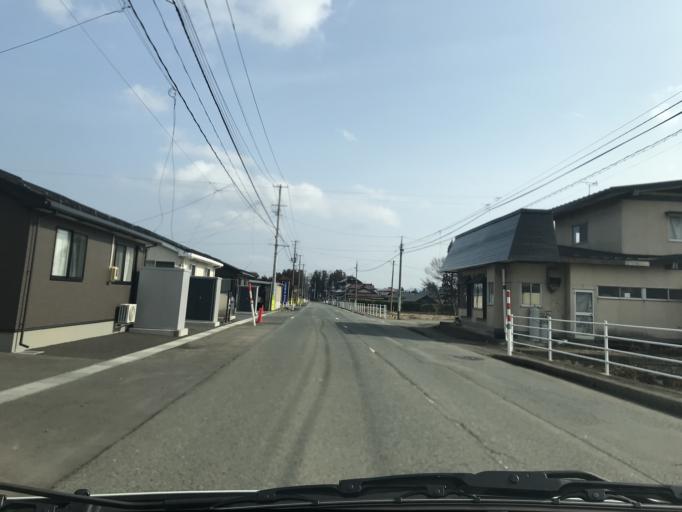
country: JP
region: Iwate
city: Kitakami
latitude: 39.2972
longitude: 141.0581
